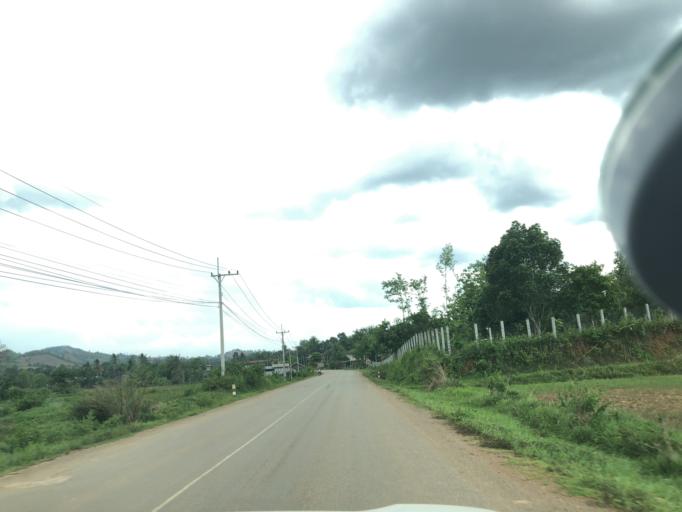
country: TH
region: Uttaradit
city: Ban Khok
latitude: 18.1162
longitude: 101.3729
